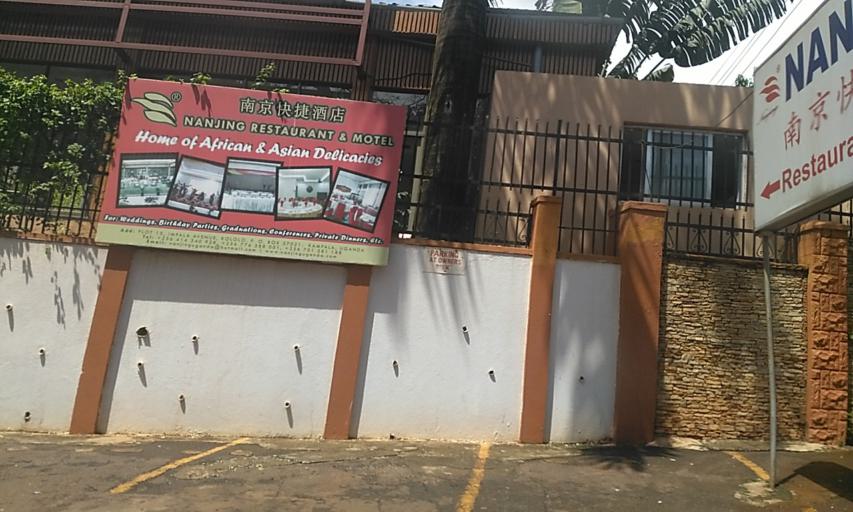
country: UG
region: Central Region
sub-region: Kampala District
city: Kampala
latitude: 0.3287
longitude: 32.5989
